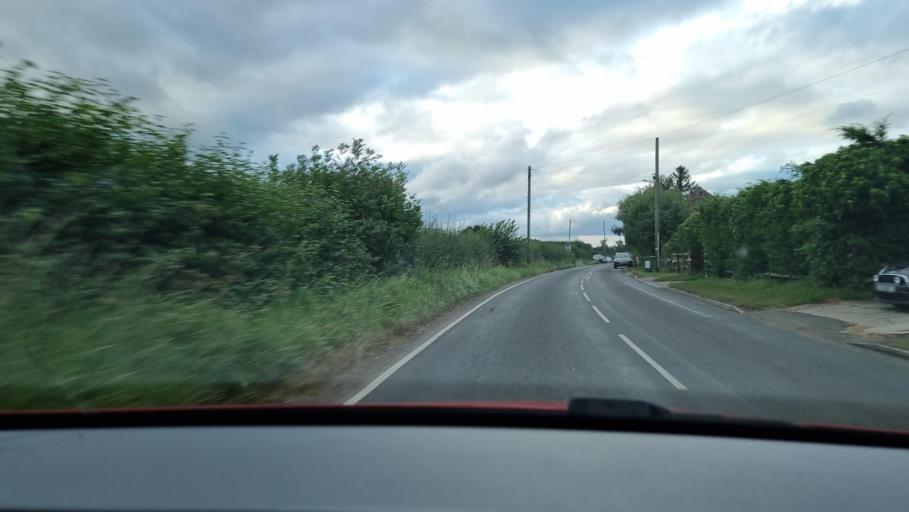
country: GB
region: England
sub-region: Buckinghamshire
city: Ivinghoe
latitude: 51.8420
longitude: -0.6378
